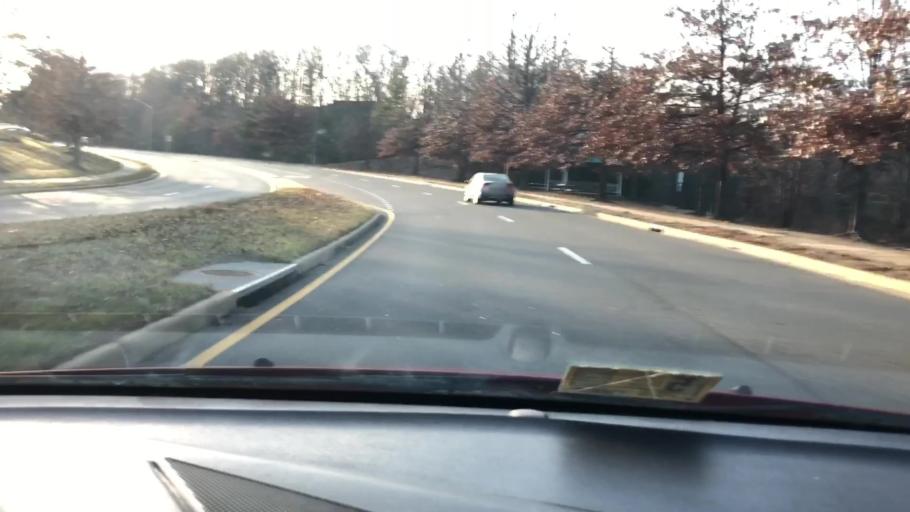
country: US
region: Virginia
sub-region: Fairfax County
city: Franconia
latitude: 38.7745
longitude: -77.1373
